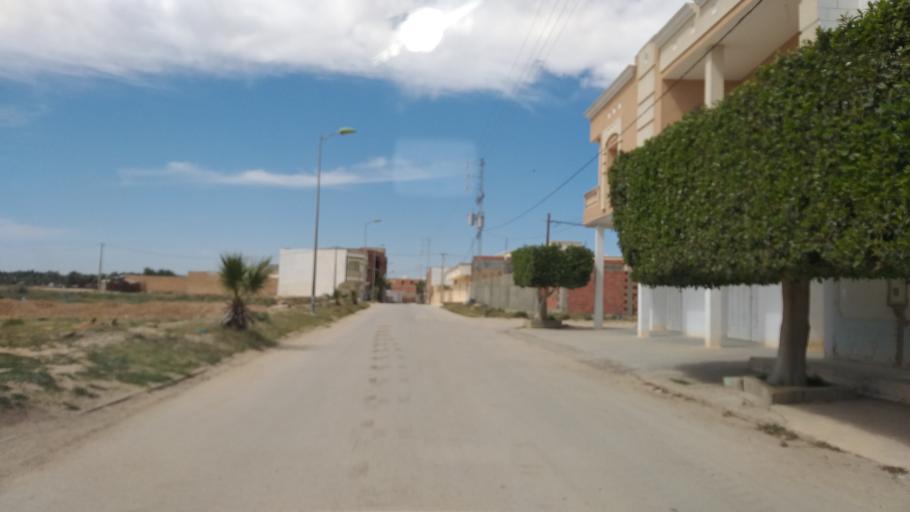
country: TN
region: Al Mahdiyah
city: El Jem
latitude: 35.3010
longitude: 10.7006
